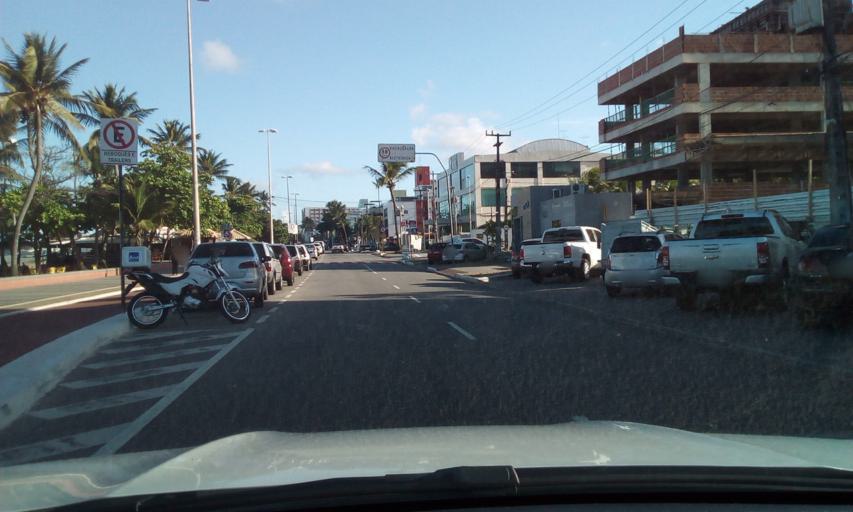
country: BR
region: Paraiba
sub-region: Joao Pessoa
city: Joao Pessoa
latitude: -7.1248
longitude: -34.8238
